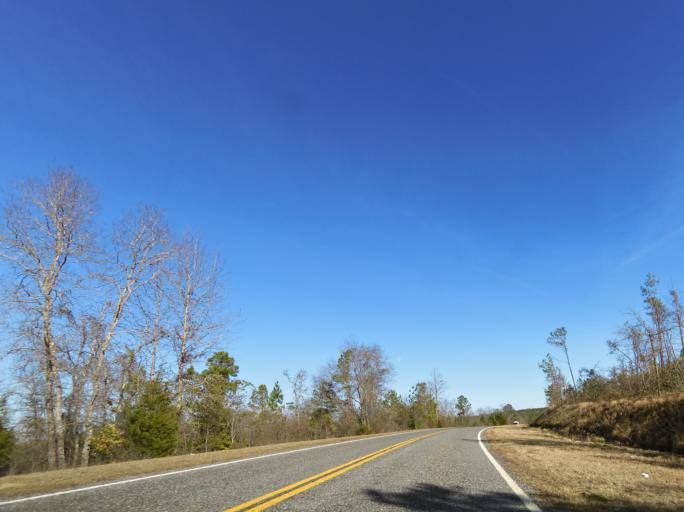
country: US
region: Georgia
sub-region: Crawford County
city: Knoxville
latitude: 32.7271
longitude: -83.9771
